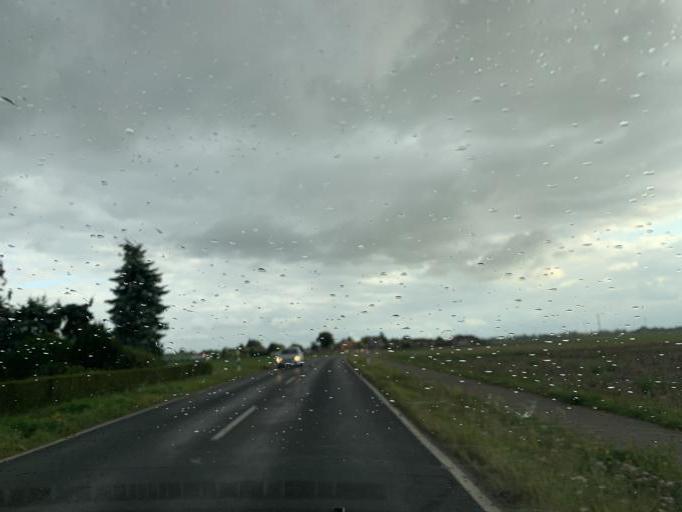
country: DE
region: North Rhine-Westphalia
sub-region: Regierungsbezirk Koln
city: Linnich
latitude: 50.9711
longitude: 6.2711
